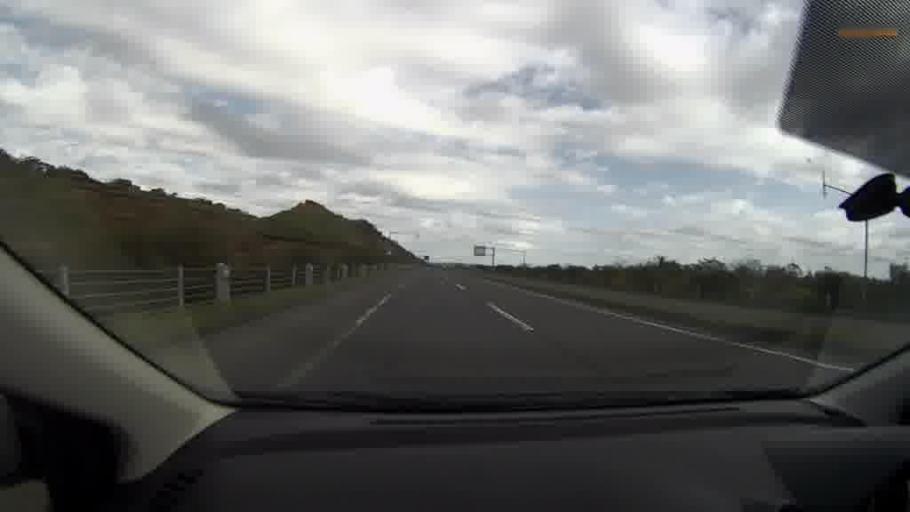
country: JP
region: Hokkaido
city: Kushiro
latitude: 43.0137
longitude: 144.2566
